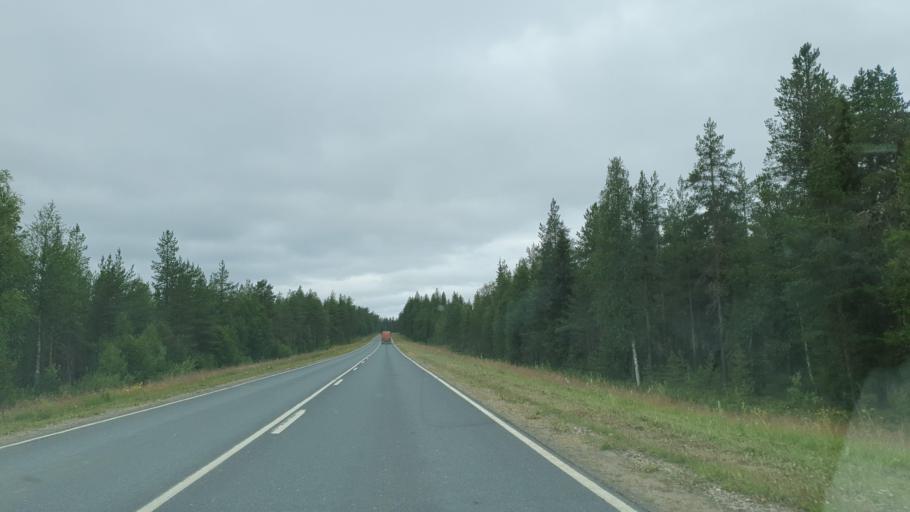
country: FI
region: Lapland
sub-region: Pohjois-Lappi
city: Sodankylae
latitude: 67.4153
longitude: 26.4848
